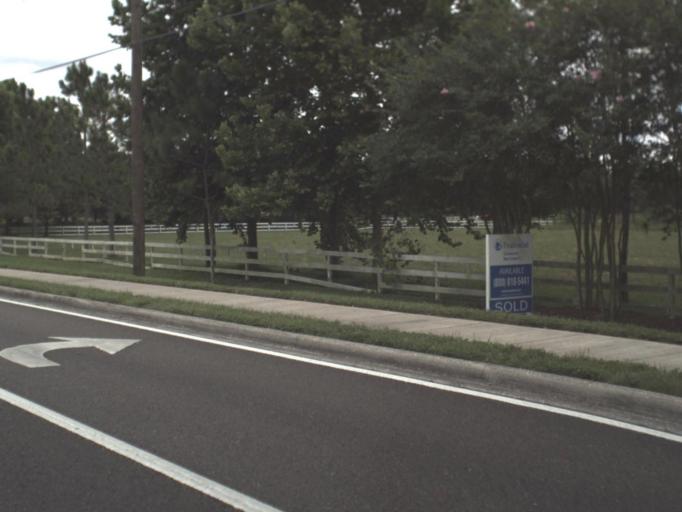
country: US
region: Florida
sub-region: Pasco County
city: Trinity
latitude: 28.1991
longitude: -82.6458
